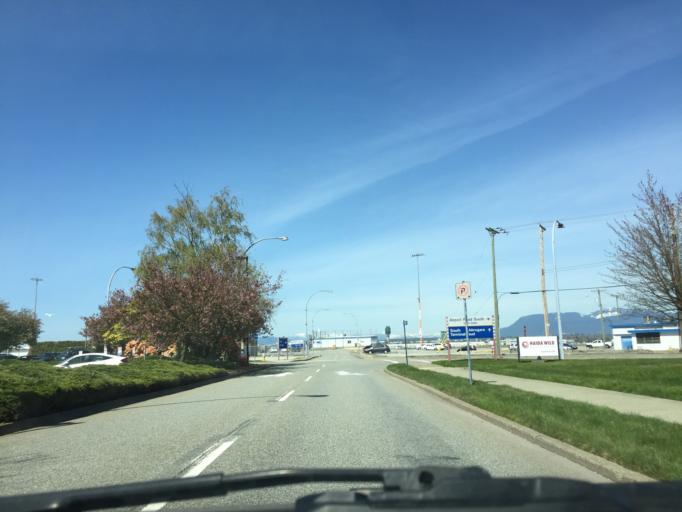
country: CA
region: British Columbia
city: Richmond
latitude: 49.1800
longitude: -123.1680
